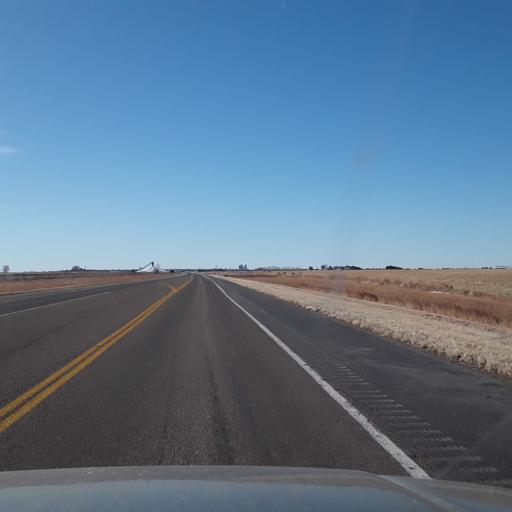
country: US
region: Nebraska
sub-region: Kearney County
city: Minden
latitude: 40.5238
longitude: -98.8955
